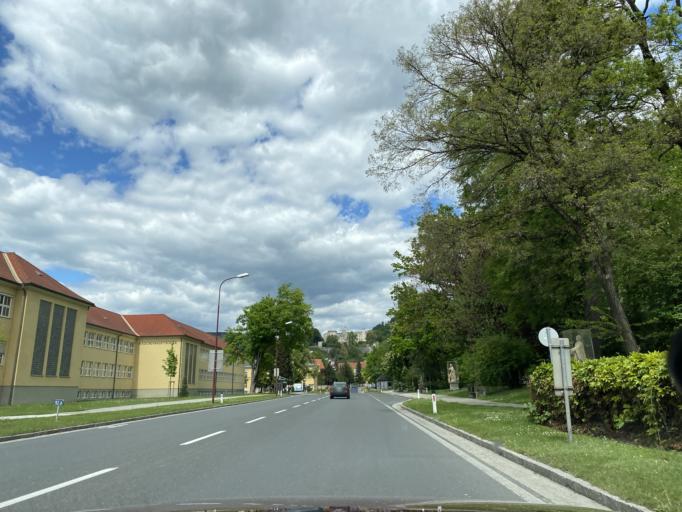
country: AT
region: Carinthia
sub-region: Politischer Bezirk Wolfsberg
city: Wolfsberg
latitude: 46.8334
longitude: 14.8429
